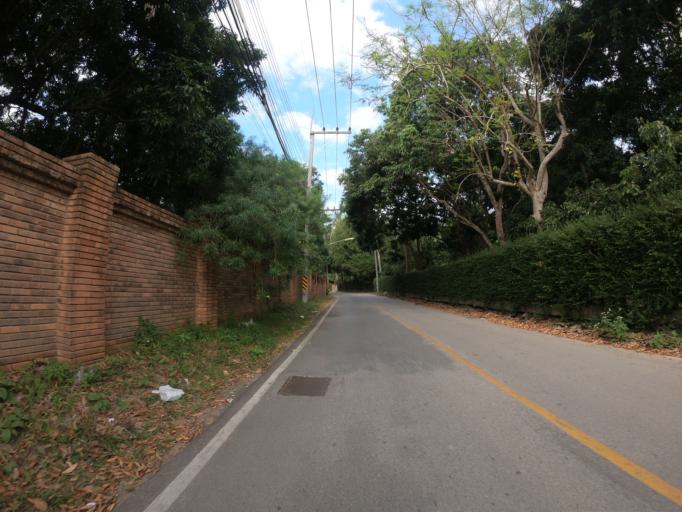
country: TH
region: Chiang Mai
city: Chiang Mai
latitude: 18.8180
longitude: 98.9536
